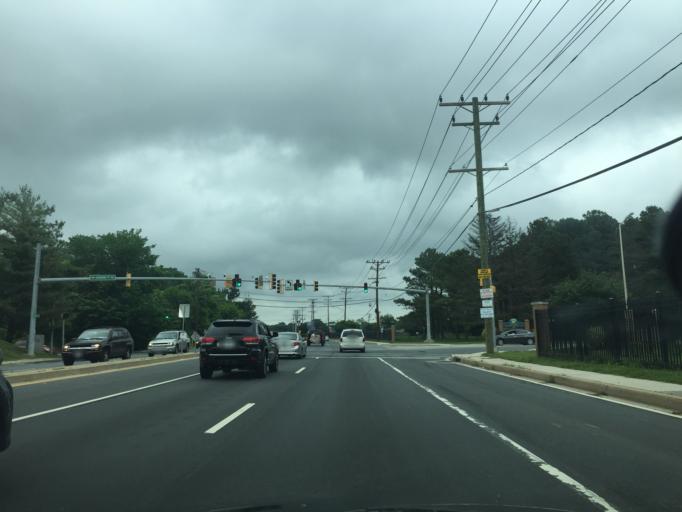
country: US
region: Maryland
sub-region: Baltimore County
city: Essex
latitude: 39.2995
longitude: -76.4951
